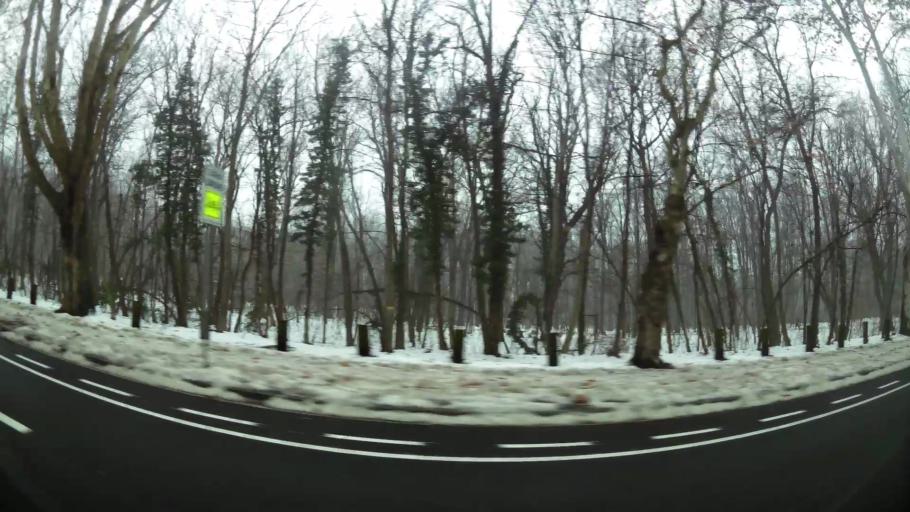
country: RS
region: Central Serbia
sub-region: Belgrade
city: Vozdovac
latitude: 44.7639
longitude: 20.4785
